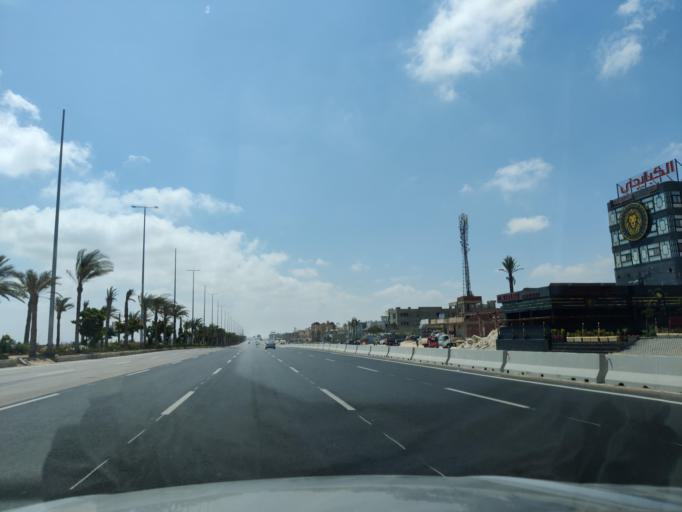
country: EG
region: Muhafazat Matruh
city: Al `Alamayn
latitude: 30.8339
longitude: 28.9622
